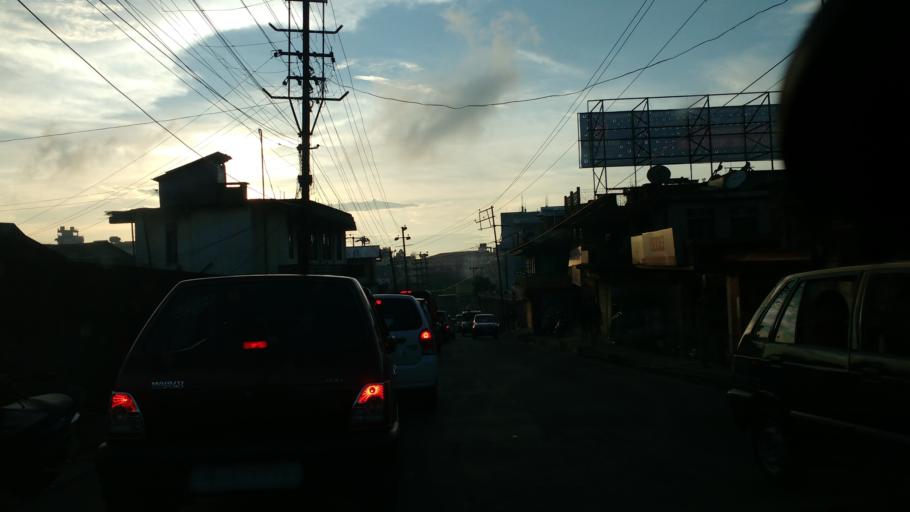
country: IN
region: Meghalaya
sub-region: East Khasi Hills
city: Shillong
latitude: 25.5639
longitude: 91.9037
